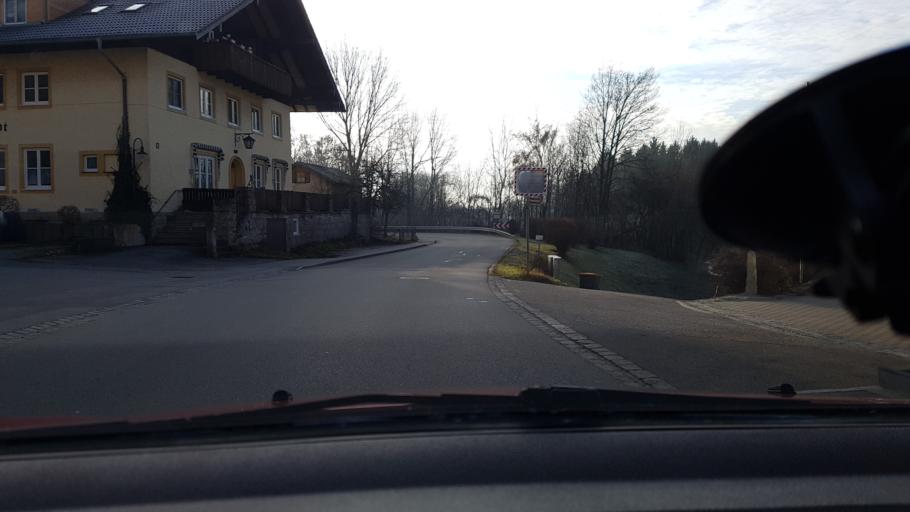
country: DE
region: Bavaria
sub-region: Lower Bavaria
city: Stubenberg
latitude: 48.2898
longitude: 13.0754
